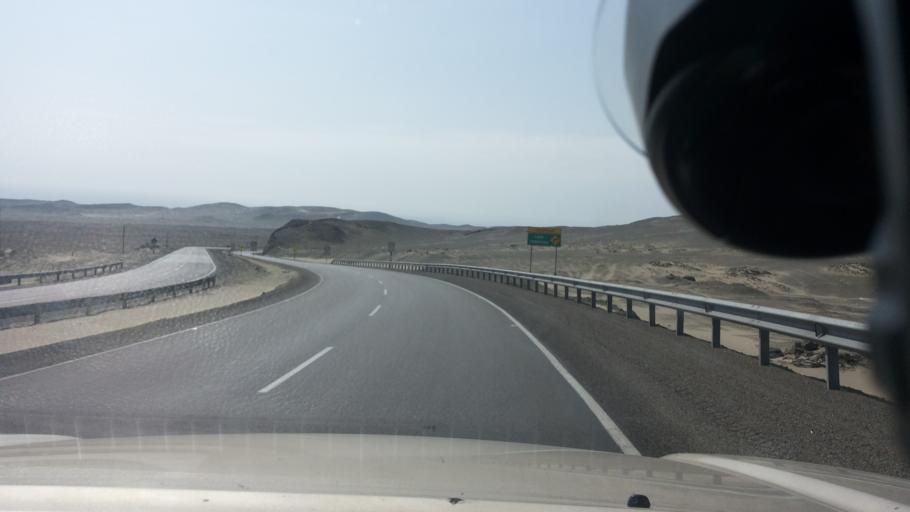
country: PE
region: Ancash
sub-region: Provincia de Huarmey
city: La Caleta Culebras
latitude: -9.7307
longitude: -78.2604
